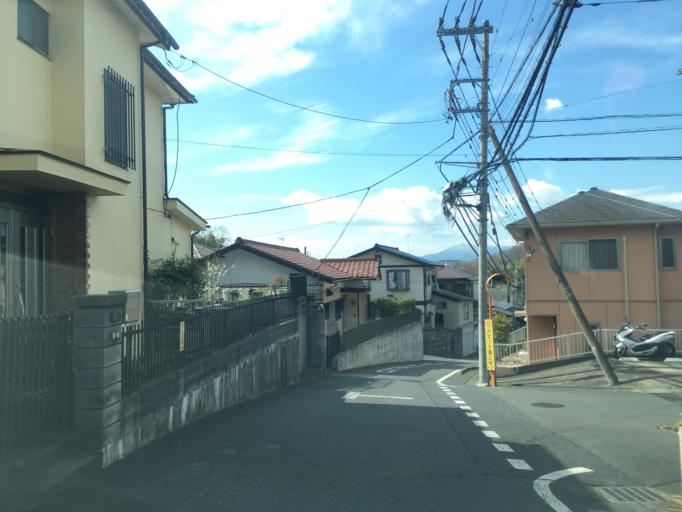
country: JP
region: Tokyo
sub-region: Machida-shi
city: Machida
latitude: 35.5879
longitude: 139.4344
